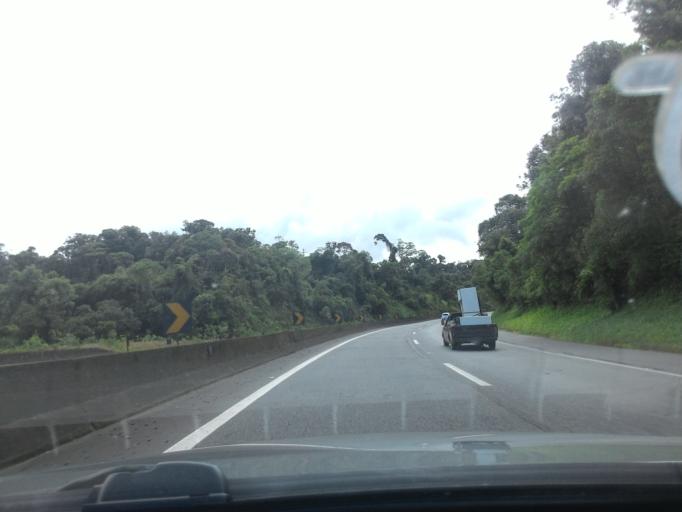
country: BR
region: Sao Paulo
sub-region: Cajati
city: Cajati
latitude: -24.9716
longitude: -48.3500
